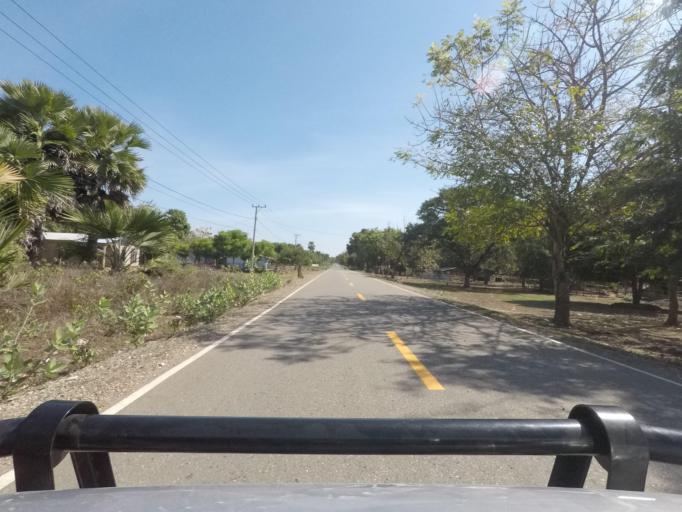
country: TL
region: Bobonaro
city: Maliana
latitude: -8.8921
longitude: 125.0147
